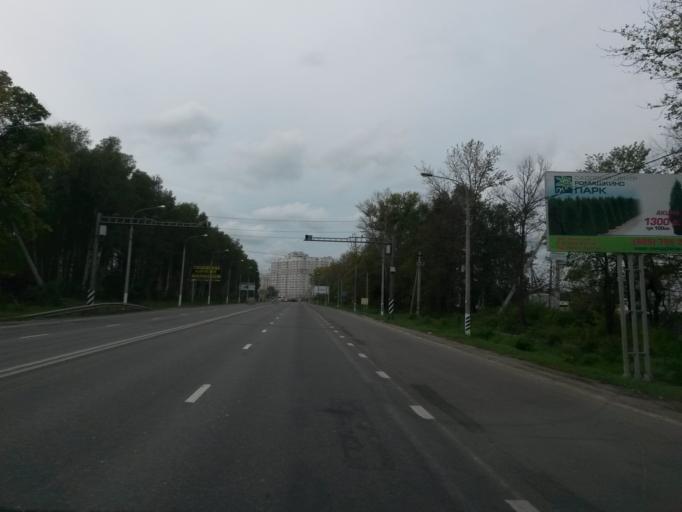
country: RU
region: Moskovskaya
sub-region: Chekhovskiy Rayon
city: Chekhov
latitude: 55.1758
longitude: 37.4778
